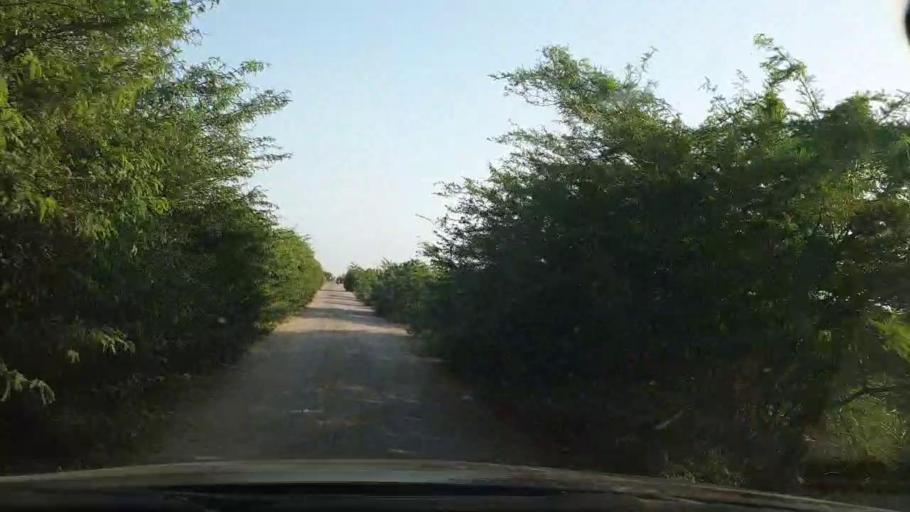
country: PK
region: Sindh
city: Naukot
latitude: 24.7646
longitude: 69.2035
